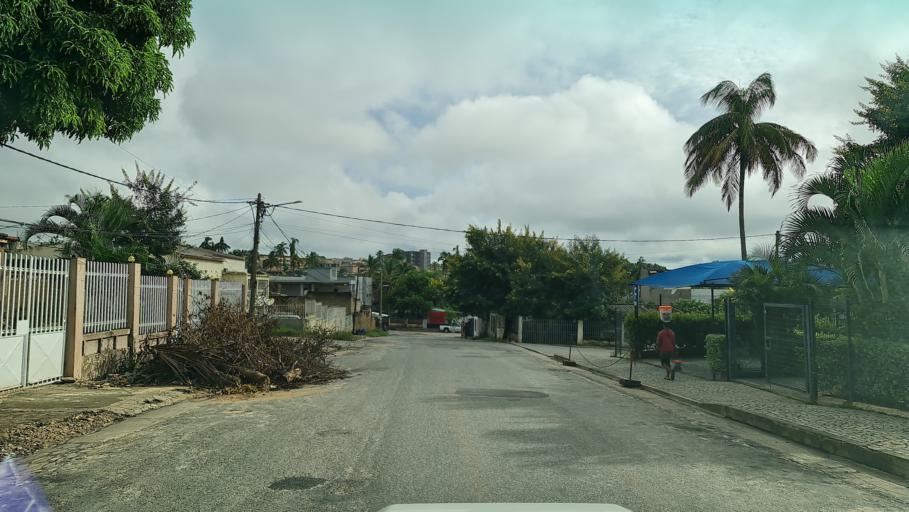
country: MZ
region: Nampula
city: Nampula
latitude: -15.1274
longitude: 39.2637
